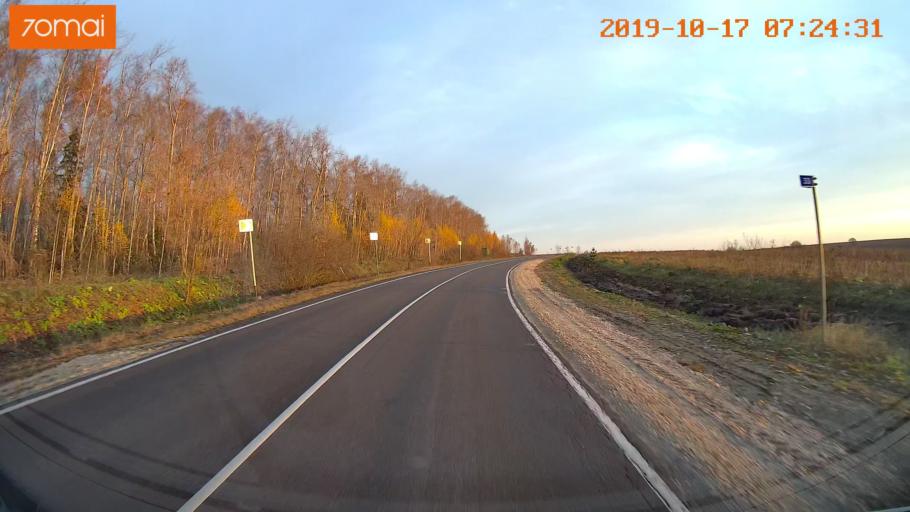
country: RU
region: Ivanovo
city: Gavrilov Posad
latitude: 56.3396
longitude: 40.1120
